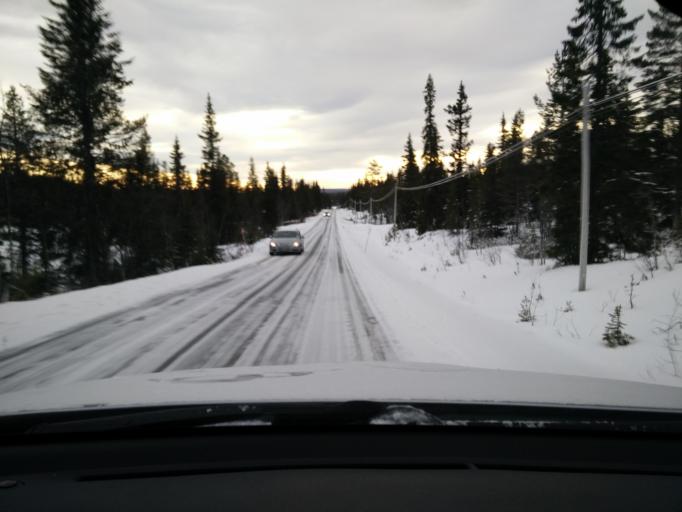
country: SE
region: Jaemtland
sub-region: Bergs Kommun
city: Hoverberg
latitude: 62.4878
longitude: 14.1189
